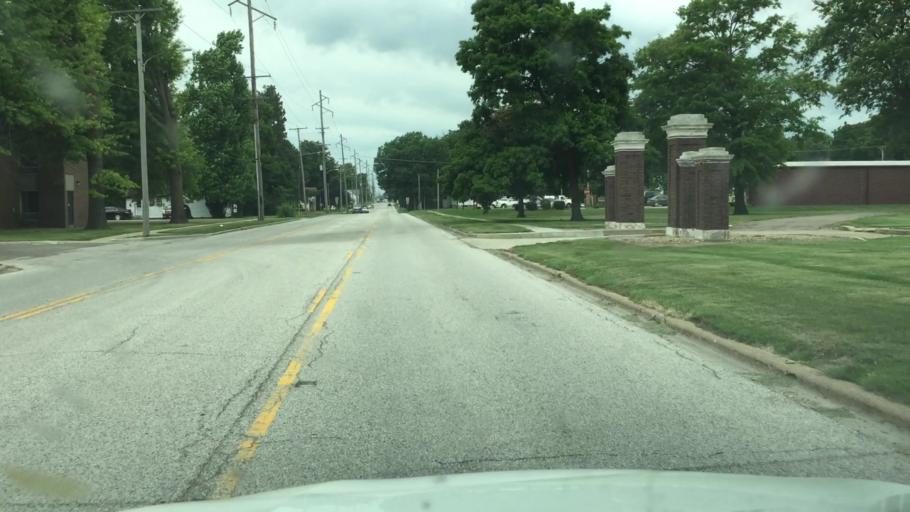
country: US
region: Illinois
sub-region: Hancock County
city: Carthage
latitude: 40.4161
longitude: -91.1255
